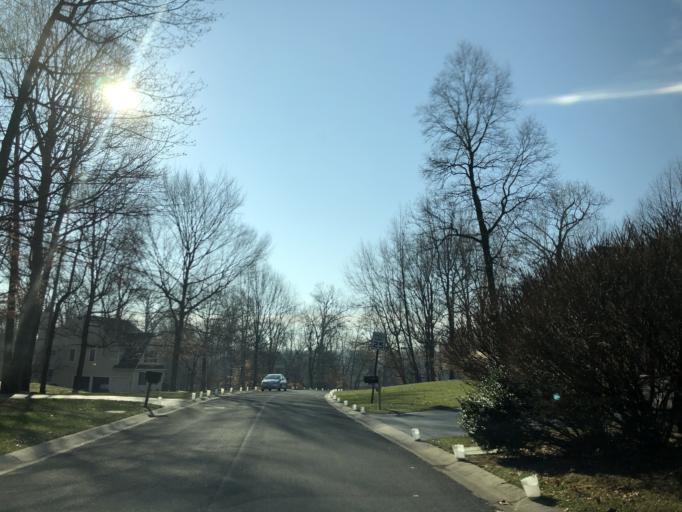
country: US
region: Pennsylvania
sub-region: Chester County
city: Downingtown
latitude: 39.9894
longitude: -75.7030
